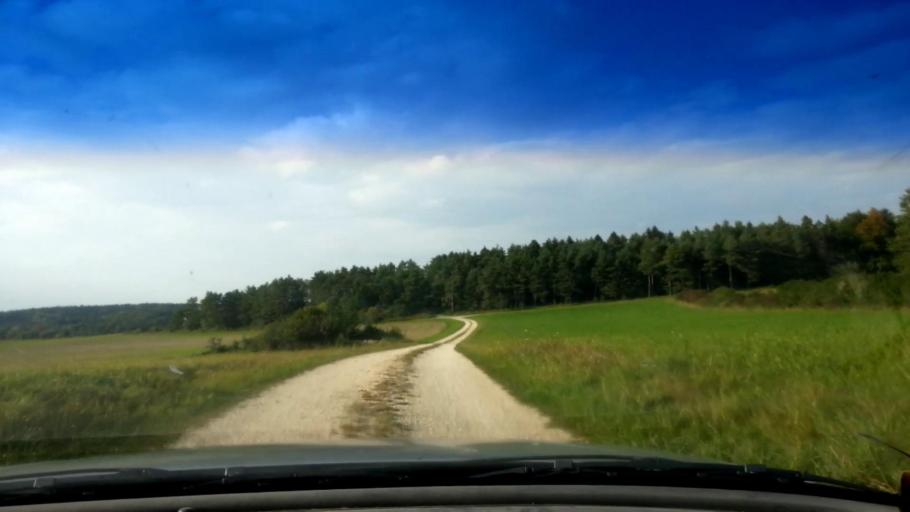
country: DE
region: Bavaria
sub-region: Upper Franconia
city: Wattendorf
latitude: 49.9986
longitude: 11.1125
